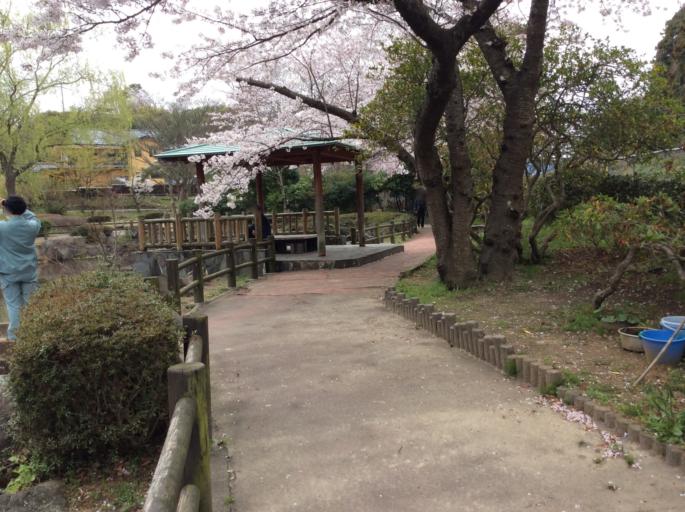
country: JP
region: Fukushima
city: Iwaki
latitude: 37.0562
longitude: 140.8826
